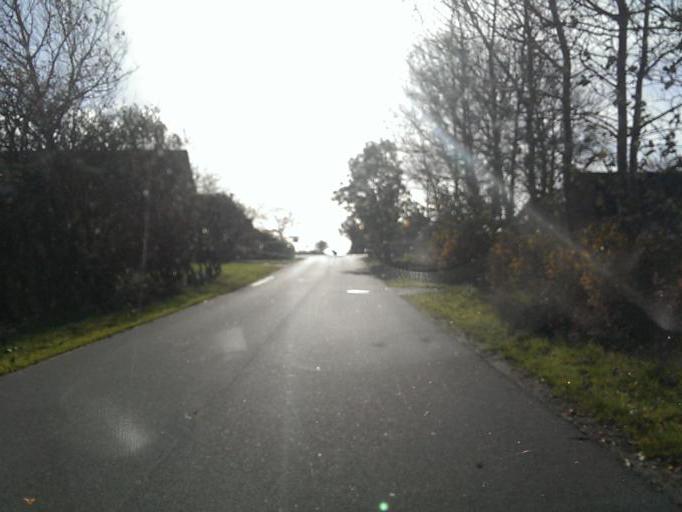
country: DK
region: South Denmark
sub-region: Esbjerg Kommune
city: Tjaereborg
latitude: 55.4601
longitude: 8.5733
